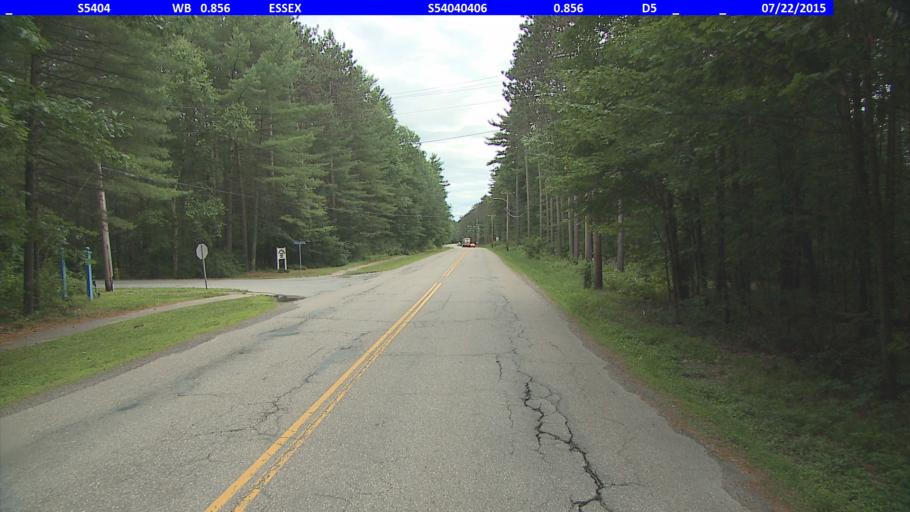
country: US
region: Vermont
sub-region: Chittenden County
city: Jericho
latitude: 44.5036
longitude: -73.0392
